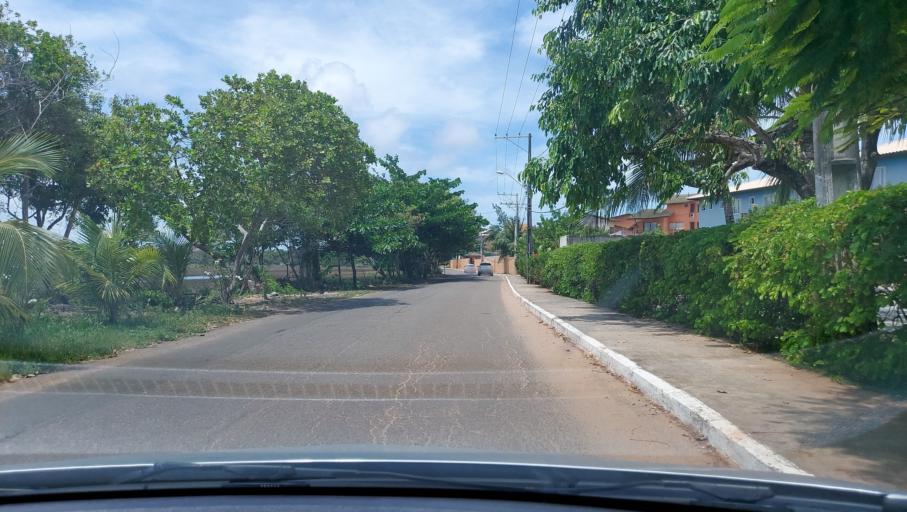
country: BR
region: Bahia
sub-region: Mata De Sao Joao
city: Mata de Sao Joao
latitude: -12.6245
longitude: -38.0481
